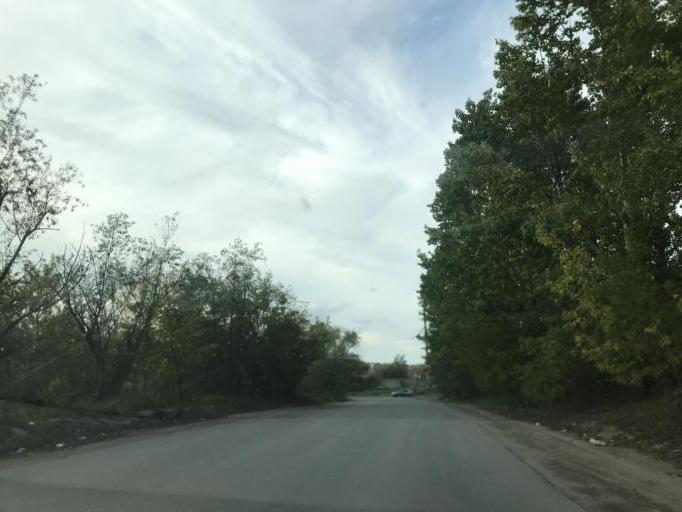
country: RU
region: Chelyabinsk
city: Dolgoderevenskoye
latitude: 55.2551
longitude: 61.3602
